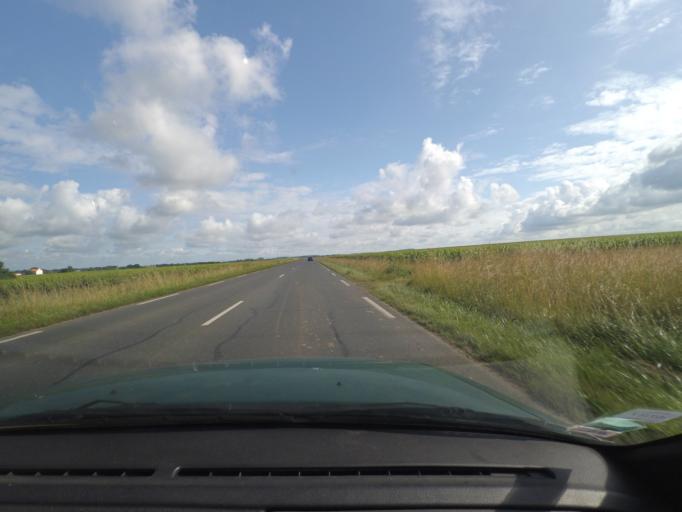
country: FR
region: Pays de la Loire
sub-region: Departement de la Loire-Atlantique
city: Mouzillon
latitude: 47.1285
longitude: -1.2826
